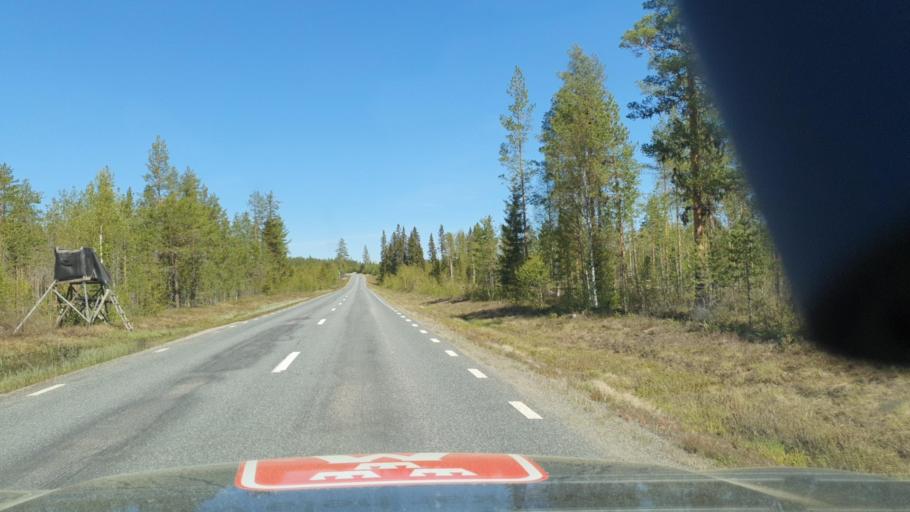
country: SE
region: Vaesternorrland
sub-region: OErnskoeldsviks Kommun
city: Bredbyn
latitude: 63.8292
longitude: 18.4769
